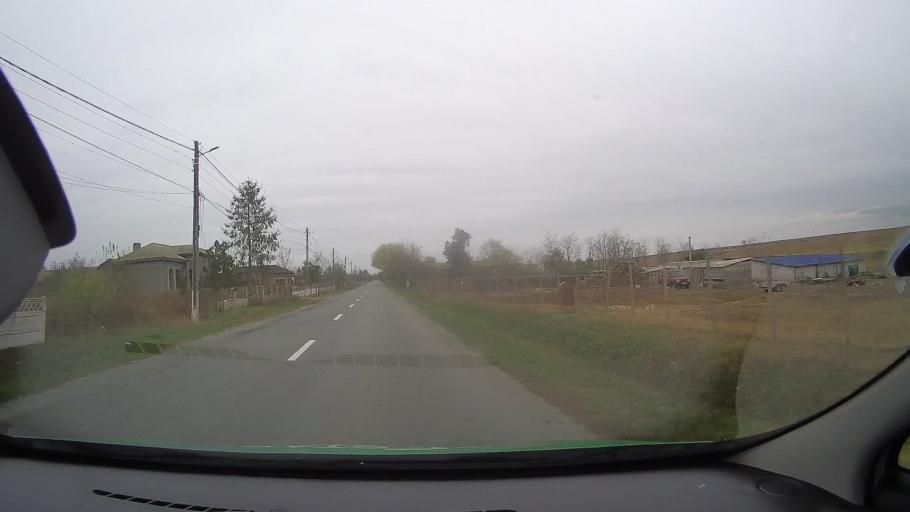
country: RO
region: Constanta
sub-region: Comuna Silistea
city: Silistea
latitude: 44.4412
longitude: 28.2317
